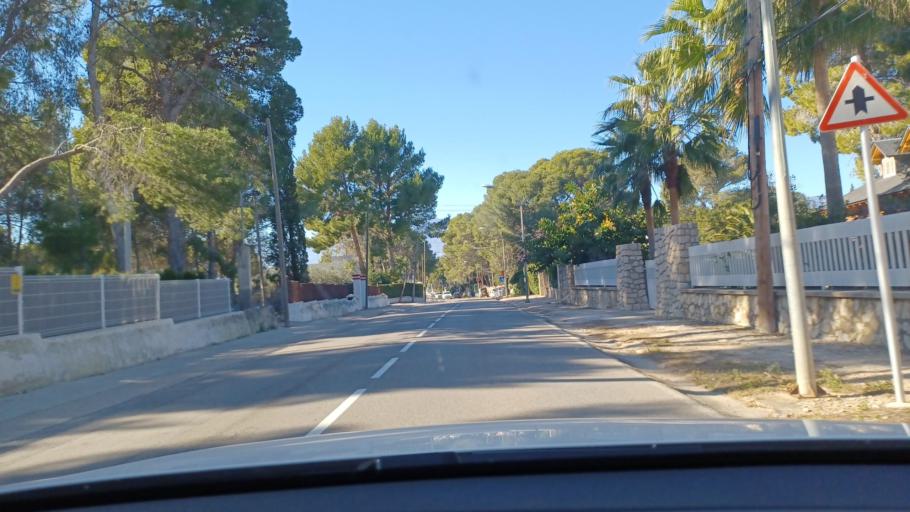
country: ES
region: Catalonia
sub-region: Provincia de Tarragona
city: Tortosa
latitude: 40.8128
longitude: 0.5343
